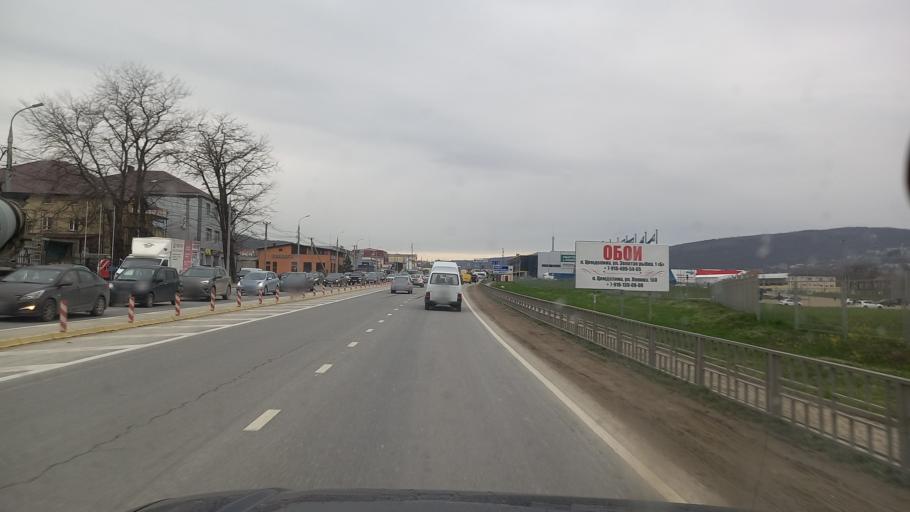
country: RU
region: Krasnodarskiy
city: Gayduk
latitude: 44.7700
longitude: 37.6983
